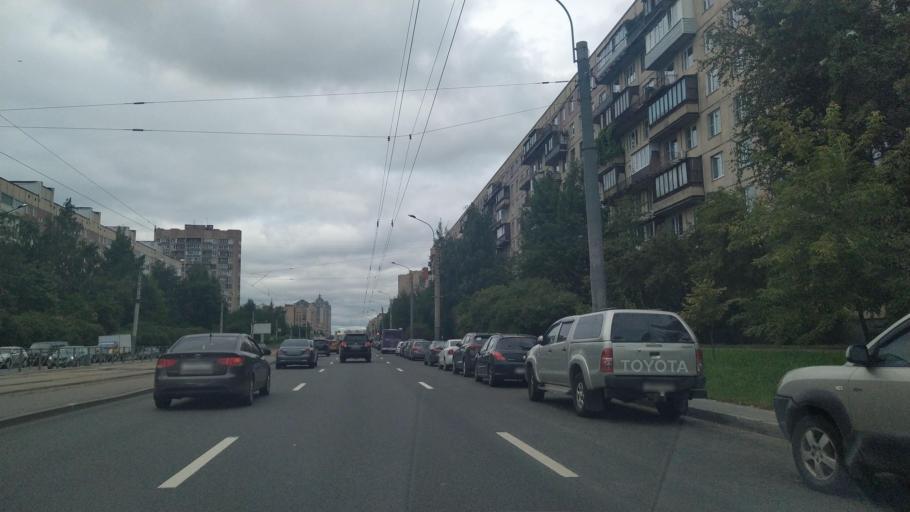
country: RU
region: St.-Petersburg
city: Sosnovka
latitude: 60.0381
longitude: 30.3571
